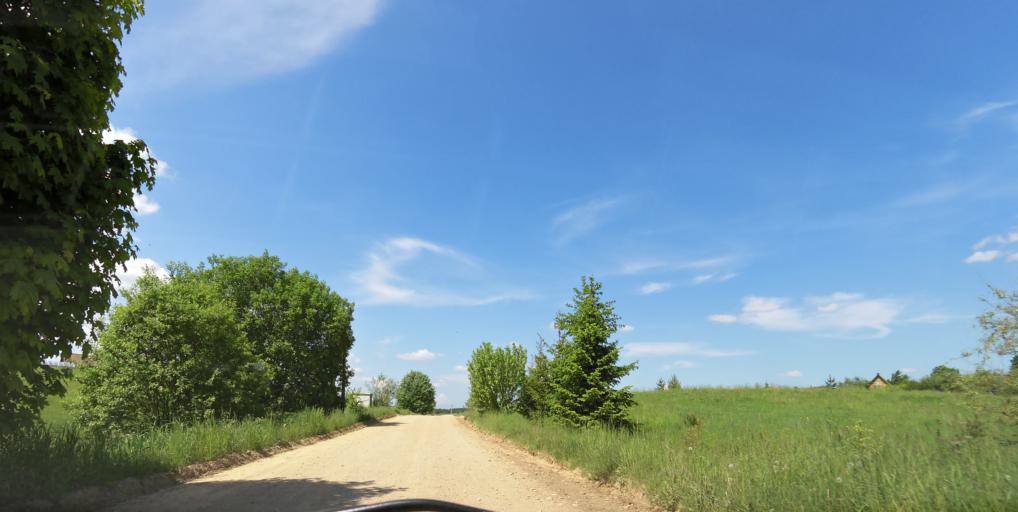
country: LT
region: Vilnius County
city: Pilaite
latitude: 54.7445
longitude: 25.1337
